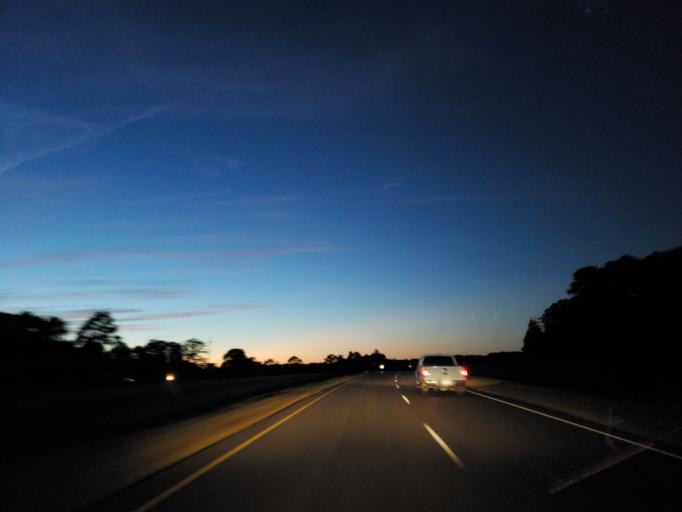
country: US
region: Mississippi
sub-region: Clarke County
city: Quitman
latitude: 32.1065
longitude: -88.7118
